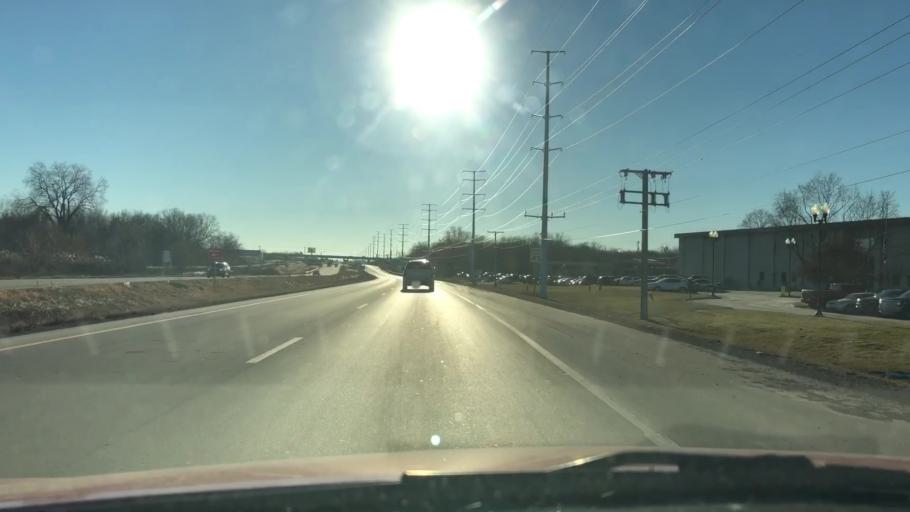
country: US
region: Wisconsin
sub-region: Brown County
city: Ashwaubenon
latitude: 44.4851
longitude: -88.0541
